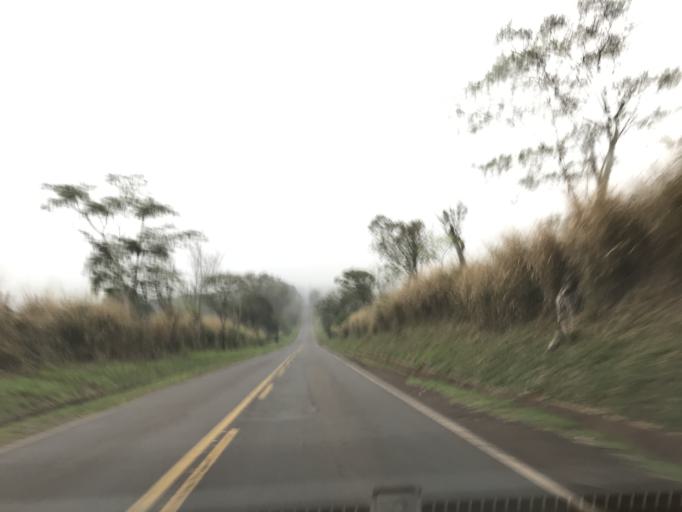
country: PY
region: Canindeyu
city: Salto del Guaira
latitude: -24.1010
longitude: -54.1027
